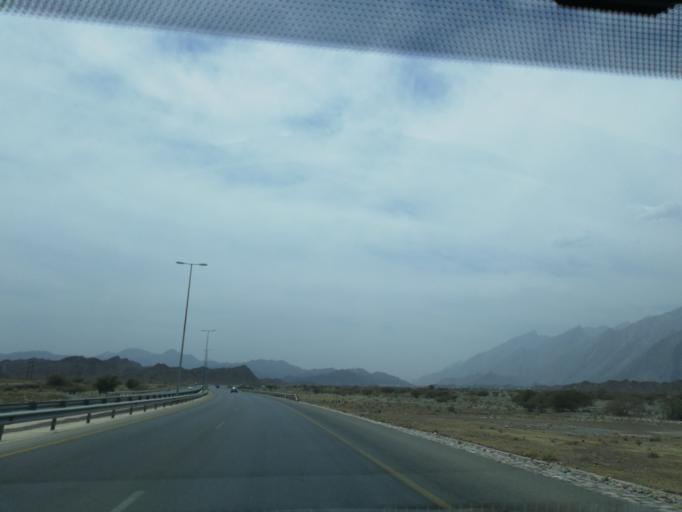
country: OM
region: Muhafazat ad Dakhiliyah
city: Sufalat Sama'il
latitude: 23.2288
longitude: 57.9031
